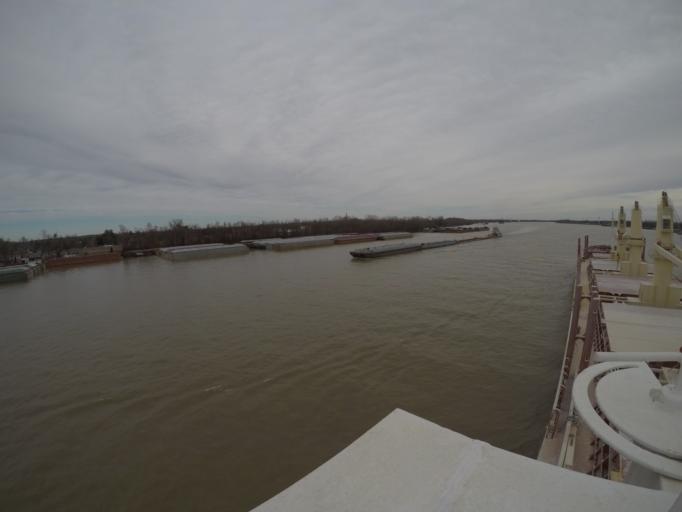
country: US
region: Louisiana
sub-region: Saint John the Baptist Parish
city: Reserve
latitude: 30.0467
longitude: -90.5351
